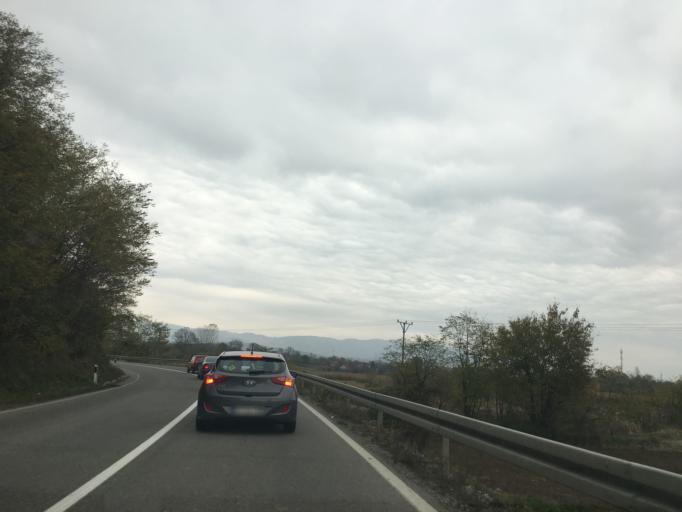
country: RS
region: Central Serbia
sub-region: Raski Okrug
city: Kraljevo
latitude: 43.7114
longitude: 20.7898
